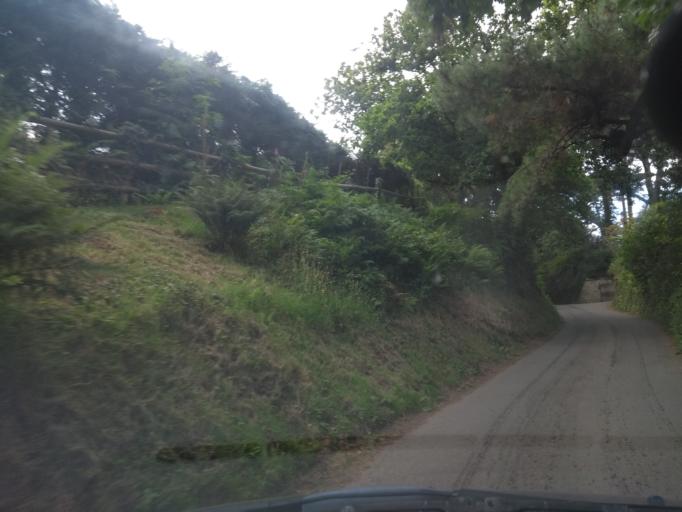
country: GB
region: England
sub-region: Devon
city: Modbury
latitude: 50.3056
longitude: -3.8525
